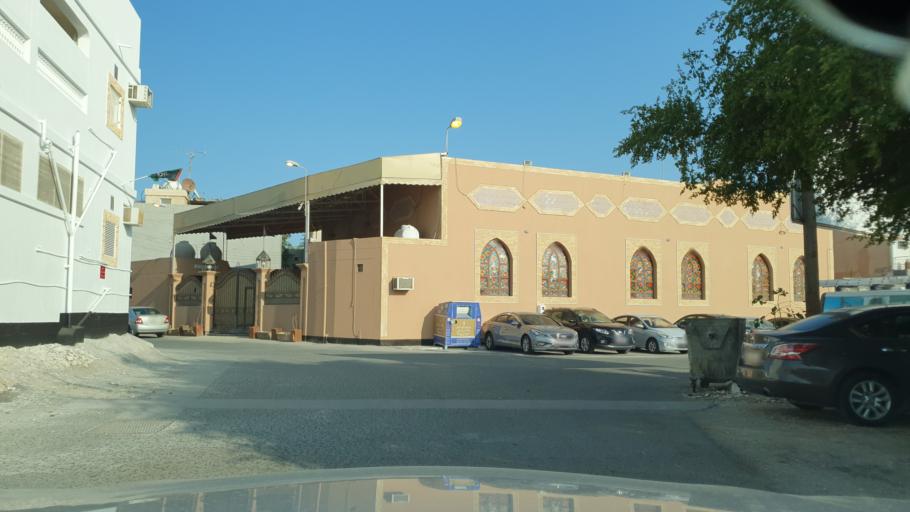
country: BH
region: Manama
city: Jidd Hafs
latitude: 26.2179
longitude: 50.4649
